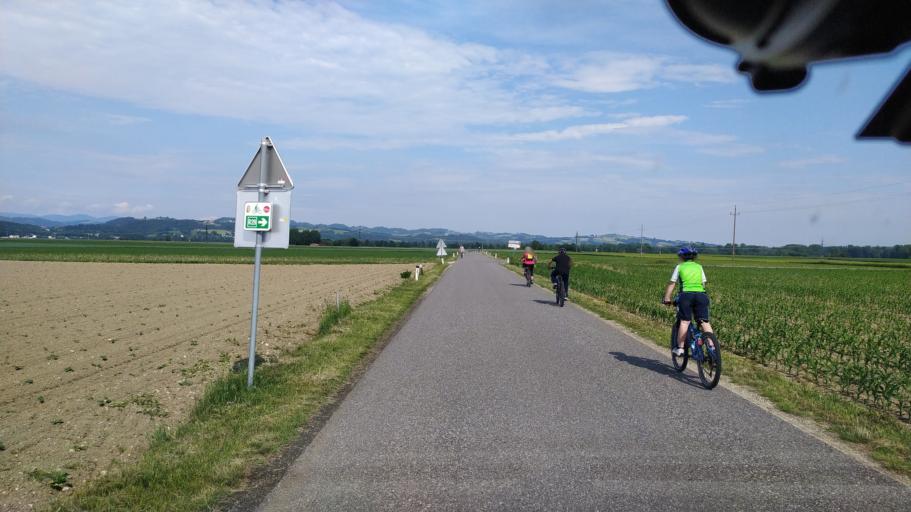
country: AT
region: Upper Austria
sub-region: Politischer Bezirk Perg
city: Bad Kreuzen
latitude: 48.1958
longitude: 14.7468
